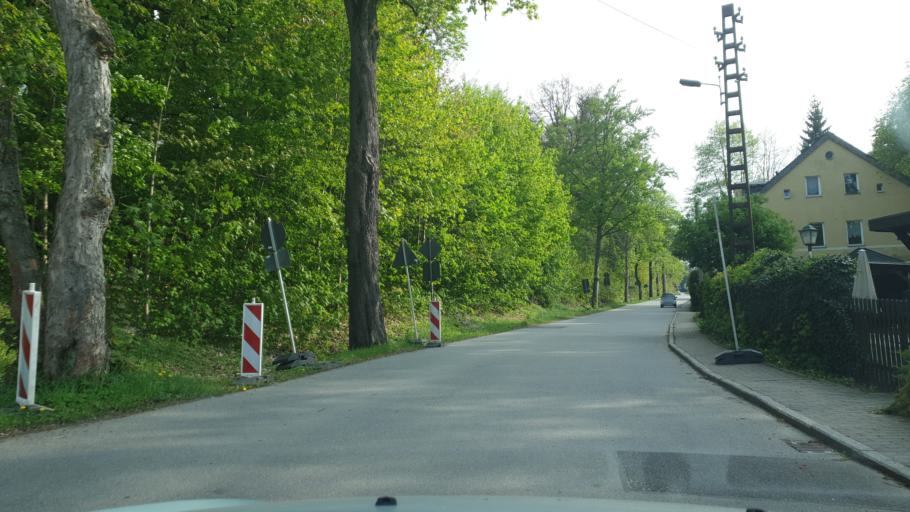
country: DE
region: Saxony
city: Stollberg
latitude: 50.7022
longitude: 12.7752
